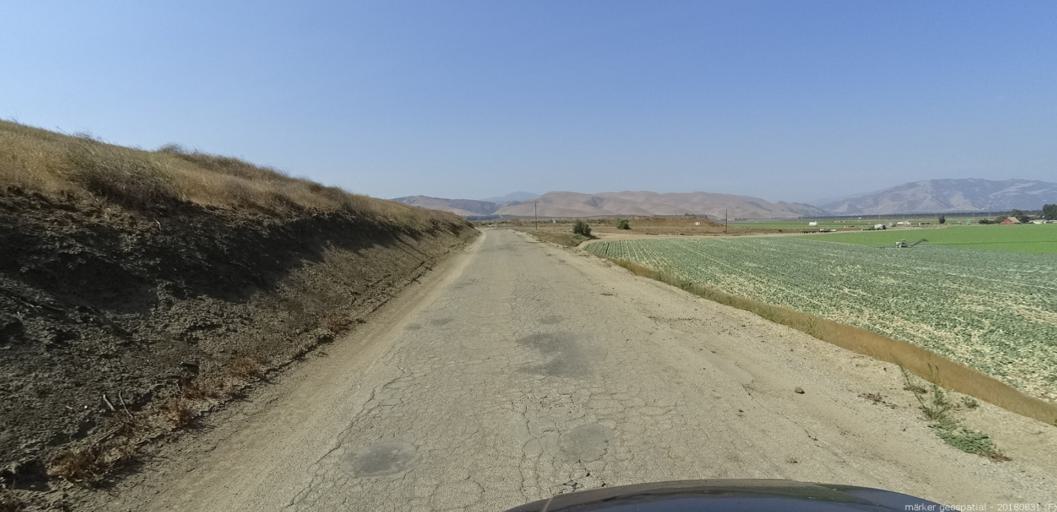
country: US
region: California
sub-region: Monterey County
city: Greenfield
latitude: 36.2988
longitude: -121.2076
